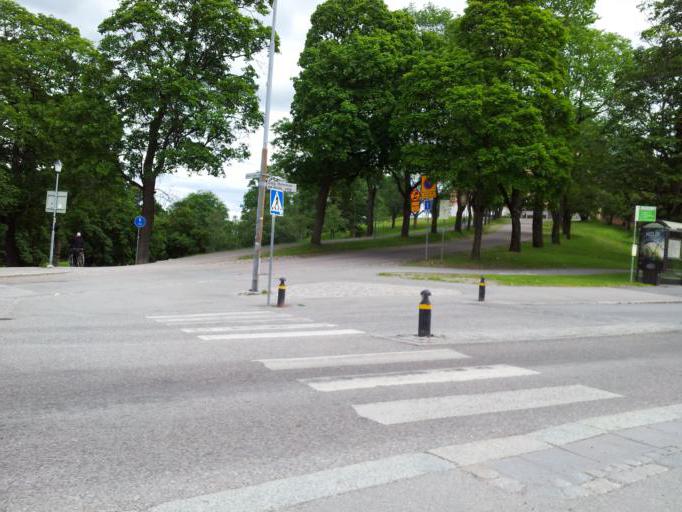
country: SE
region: Uppsala
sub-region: Uppsala Kommun
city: Uppsala
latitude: 59.8551
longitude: 17.6321
